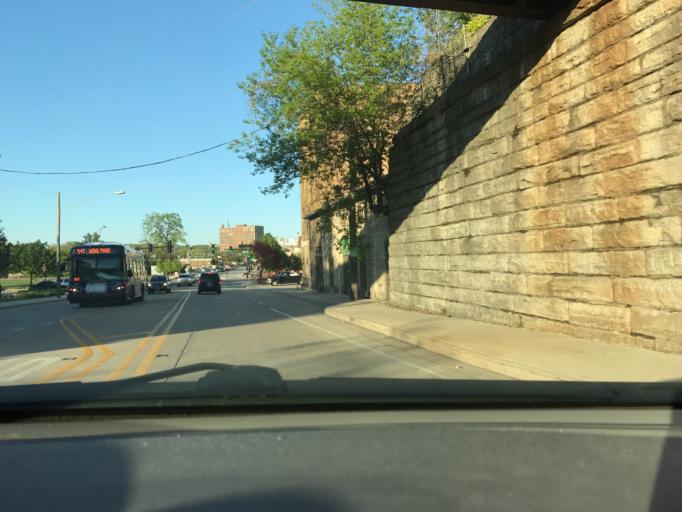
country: US
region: Illinois
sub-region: Kane County
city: Elgin
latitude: 42.0367
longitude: -88.2890
